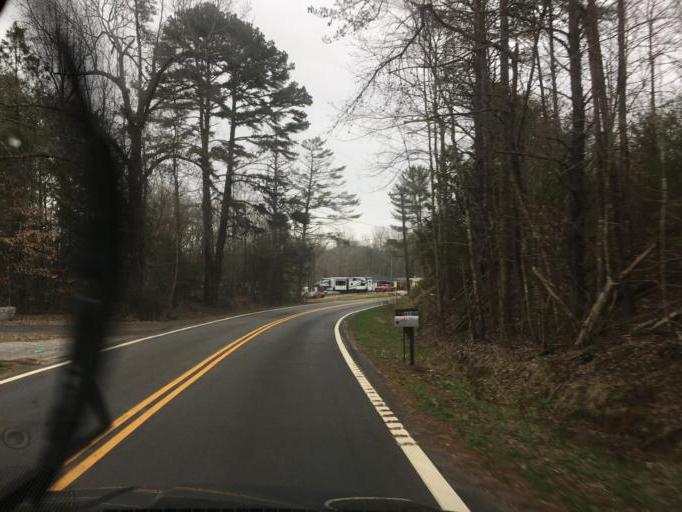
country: US
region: South Carolina
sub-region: Greenville County
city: Berea
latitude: 34.9307
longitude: -82.4987
